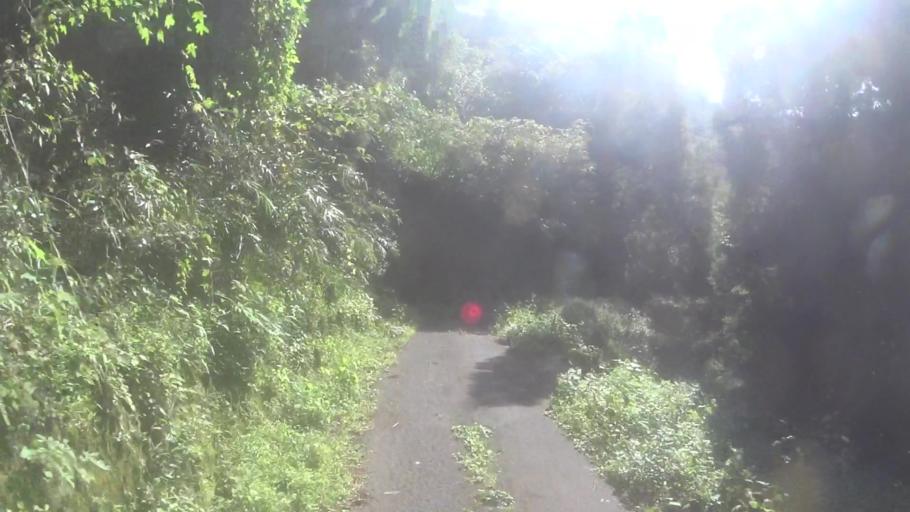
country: JP
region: Kyoto
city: Miyazu
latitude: 35.7104
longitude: 135.1624
